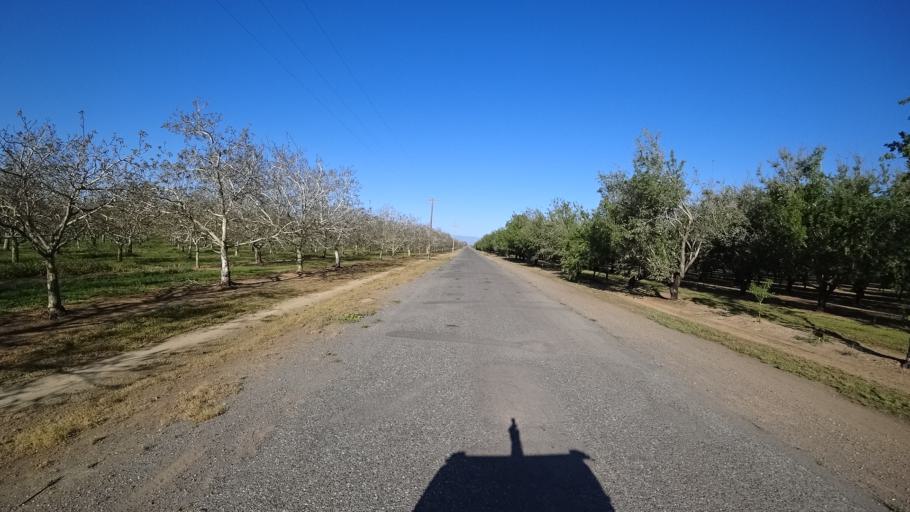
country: US
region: California
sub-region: Glenn County
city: Orland
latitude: 39.6819
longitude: -122.1616
